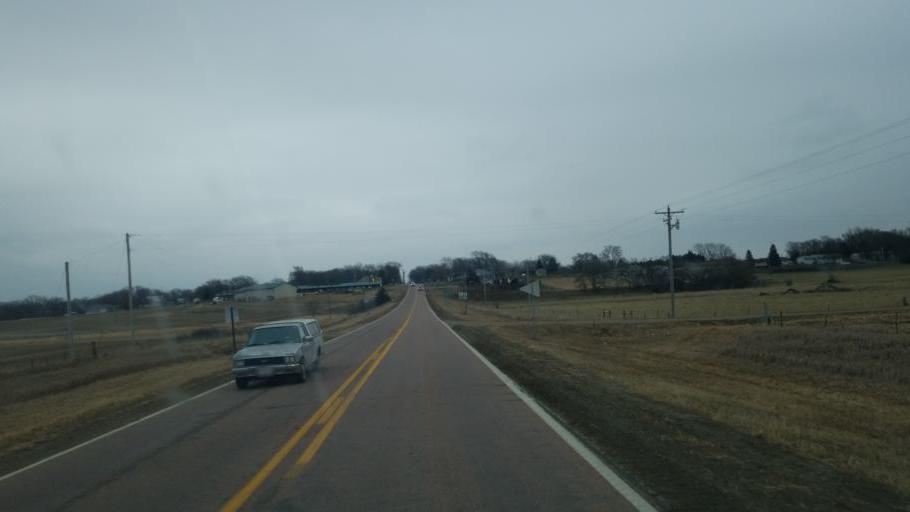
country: US
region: South Dakota
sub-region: Yankton County
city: Yankton
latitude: 42.7287
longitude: -97.5104
